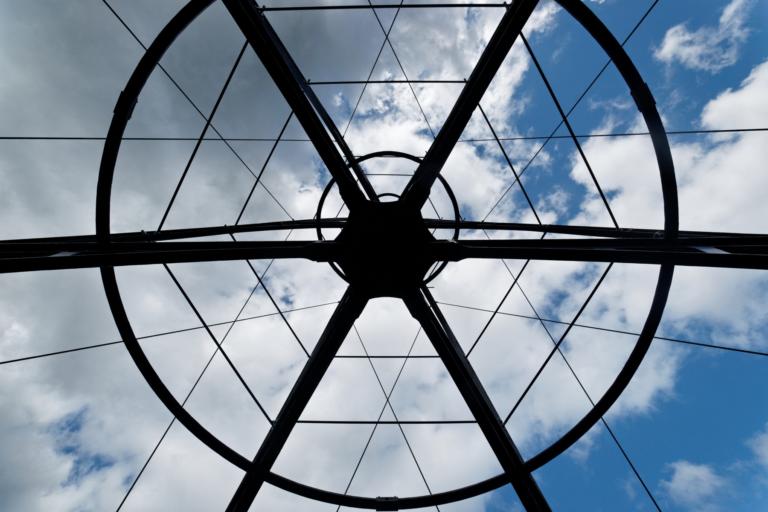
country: NL
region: North Holland
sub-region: Gemeente Texel
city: Den Burg
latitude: 53.0784
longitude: 4.8964
